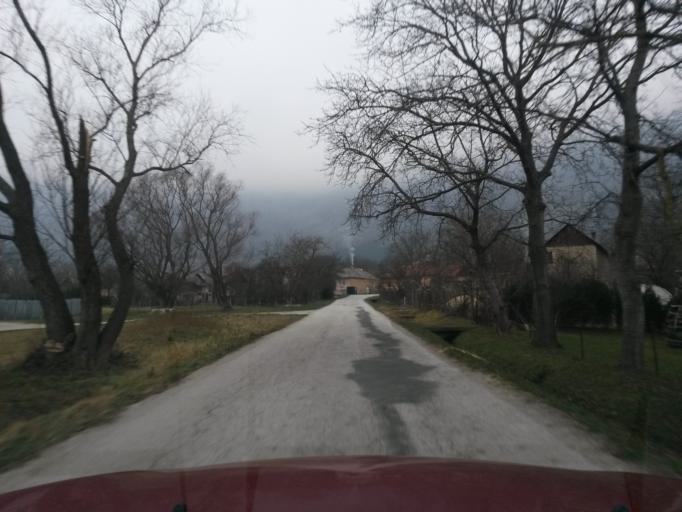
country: SK
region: Kosicky
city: Medzev
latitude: 48.6040
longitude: 20.7568
